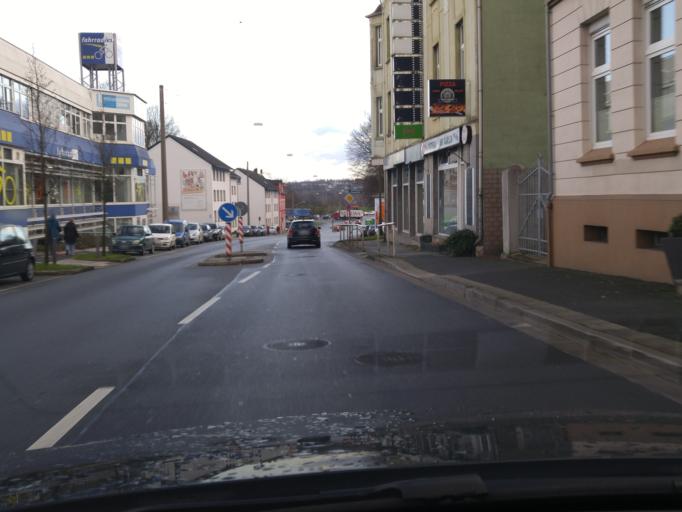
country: DE
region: North Rhine-Westphalia
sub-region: Regierungsbezirk Dusseldorf
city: Essen
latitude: 51.4281
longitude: 7.0517
